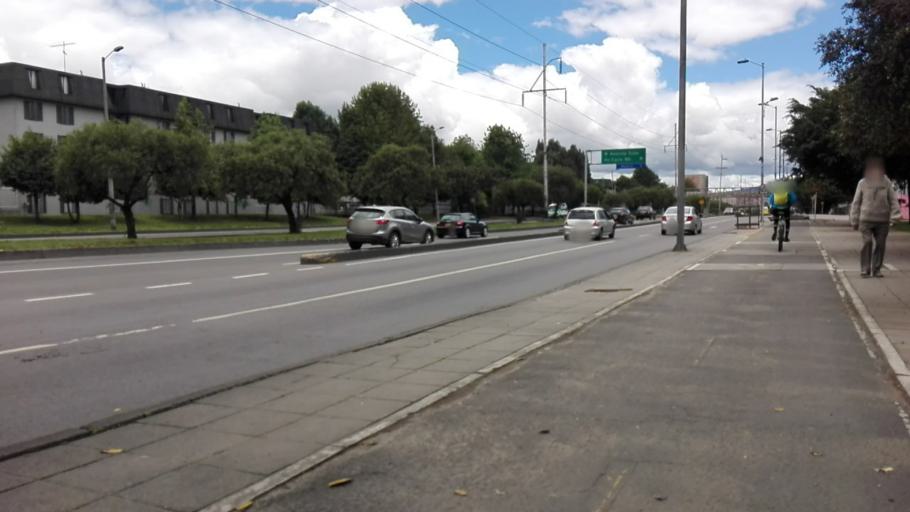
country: CO
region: Bogota D.C.
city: Barrio San Luis
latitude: 4.6799
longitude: -74.0835
